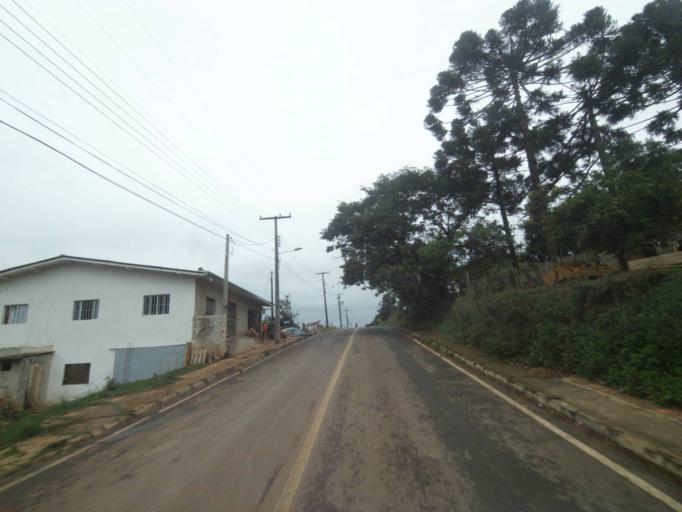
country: BR
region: Parana
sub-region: Telemaco Borba
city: Telemaco Borba
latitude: -24.3197
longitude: -50.6541
